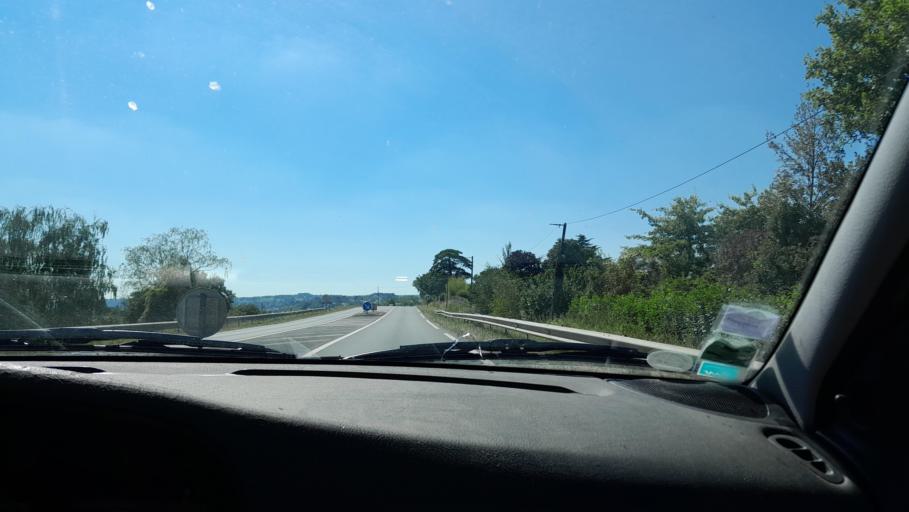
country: FR
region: Pays de la Loire
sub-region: Departement de Maine-et-Loire
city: Champtoceaux
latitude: 47.3530
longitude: -1.2579
